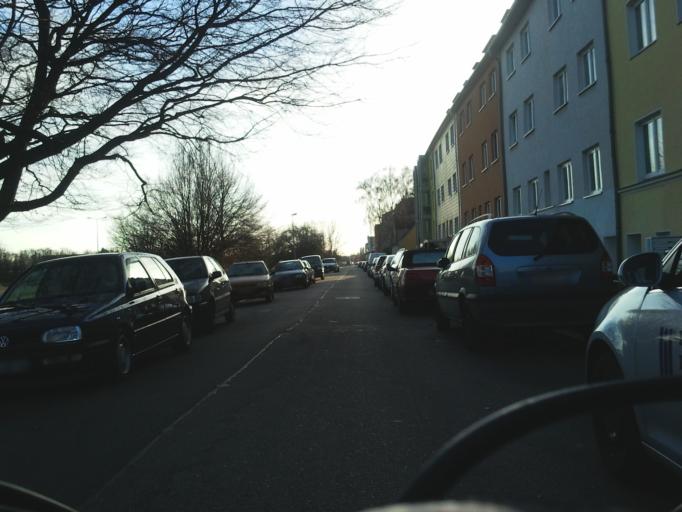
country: DE
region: Mecklenburg-Vorpommern
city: Dierkow-Neu
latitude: 54.0945
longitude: 12.1663
